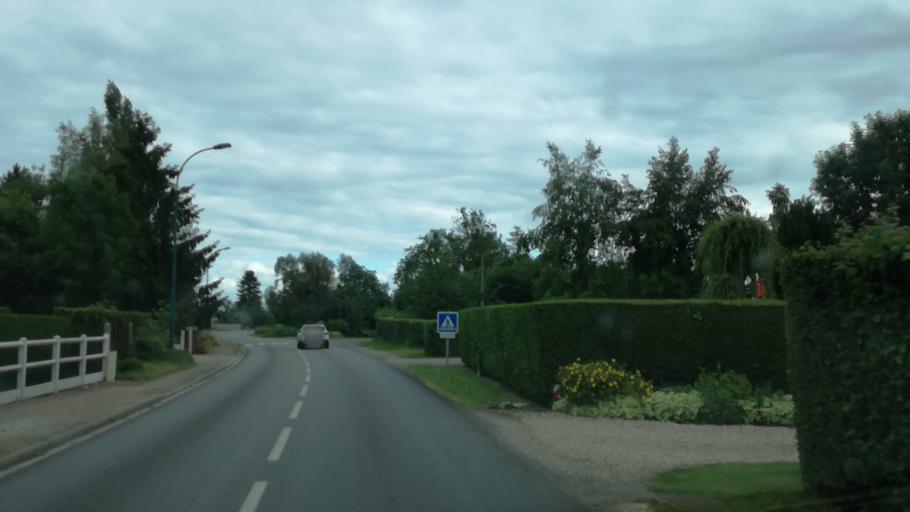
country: FR
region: Haute-Normandie
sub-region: Departement de l'Eure
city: Bourgtheroulde-Infreville
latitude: 49.2222
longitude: 0.8422
